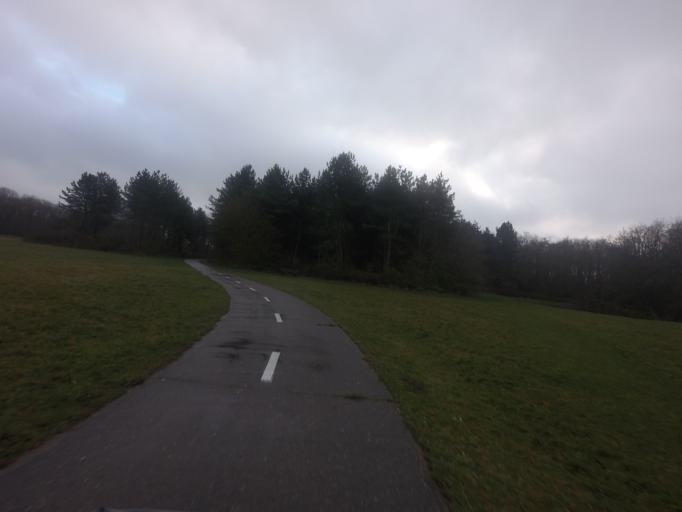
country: NL
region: North Holland
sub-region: Gemeente Texel
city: Den Burg
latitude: 53.1526
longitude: 4.8634
